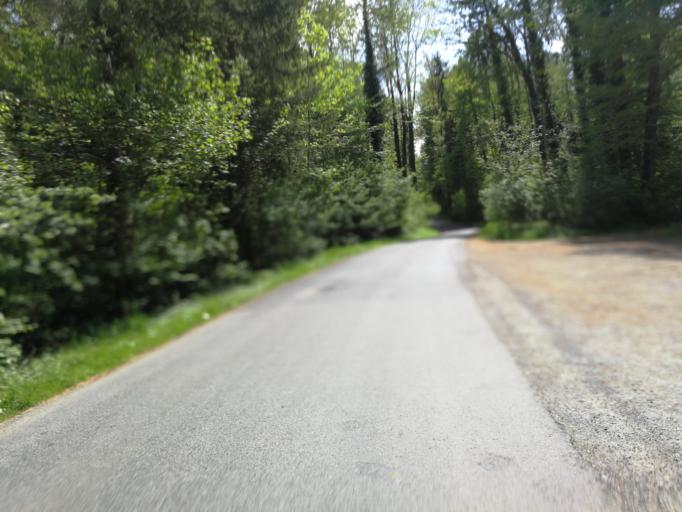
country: CH
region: Zurich
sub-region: Bezirk Hinwil
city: Binzikon
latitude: 47.2916
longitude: 8.7568
